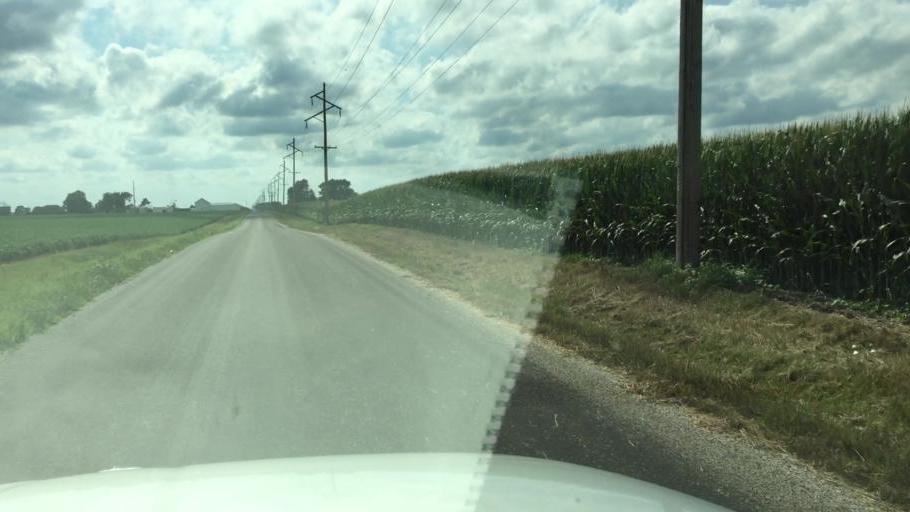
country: US
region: Illinois
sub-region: Hancock County
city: Carthage
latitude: 40.4168
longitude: -91.1710
